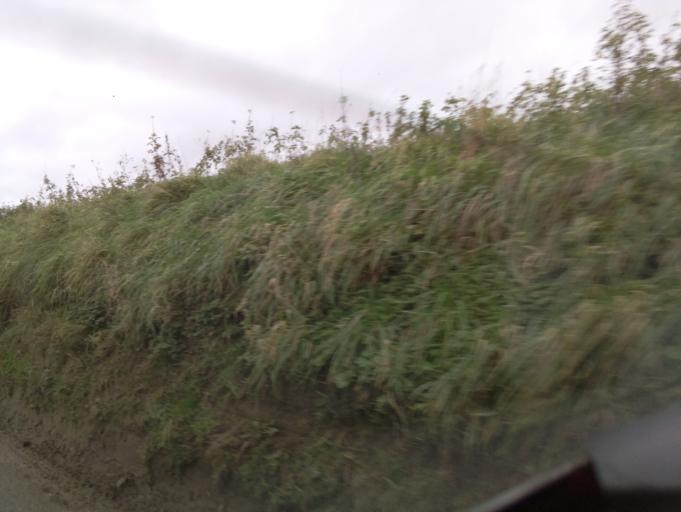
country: GB
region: England
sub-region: Somerset
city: South Petherton
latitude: 50.9449
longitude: -2.8570
